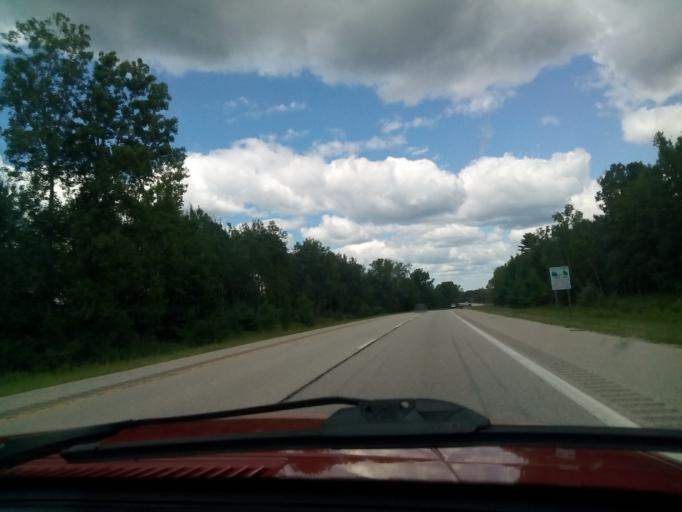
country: US
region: Michigan
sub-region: Ogemaw County
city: Skidway Lake
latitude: 44.0667
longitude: -84.0878
